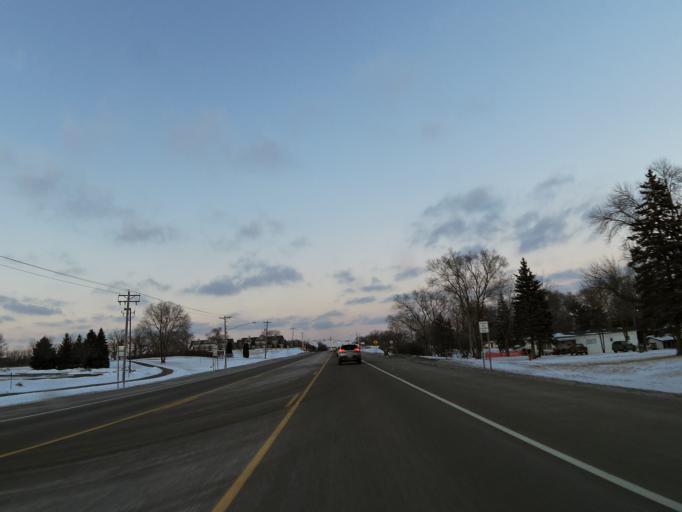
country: US
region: Minnesota
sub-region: Dakota County
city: Rosemount
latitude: 44.7475
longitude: -93.1260
